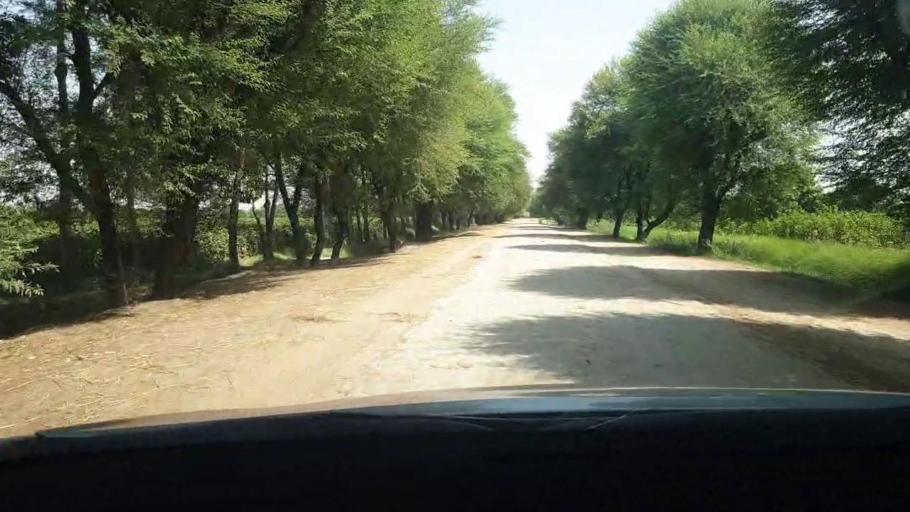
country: PK
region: Sindh
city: Tando Mittha Khan
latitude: 25.8467
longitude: 69.4424
